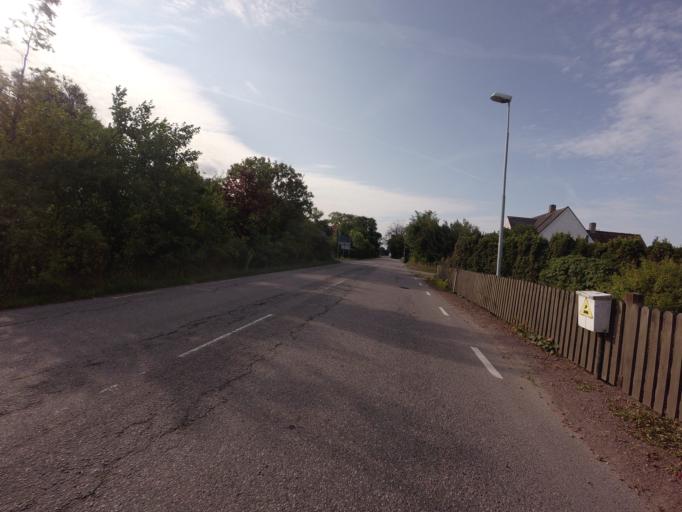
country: SE
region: Skane
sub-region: Hoganas Kommun
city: Hoganas
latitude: 56.1880
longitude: 12.6283
